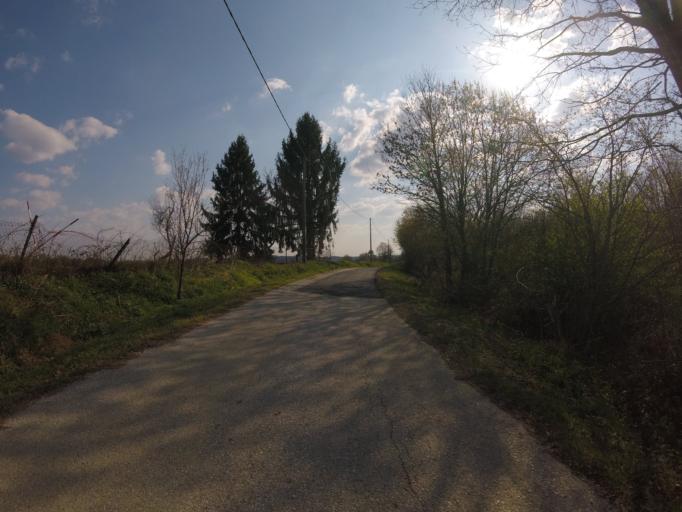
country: HR
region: Sisacko-Moslavacka
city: Glina
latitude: 45.4968
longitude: 16.0044
